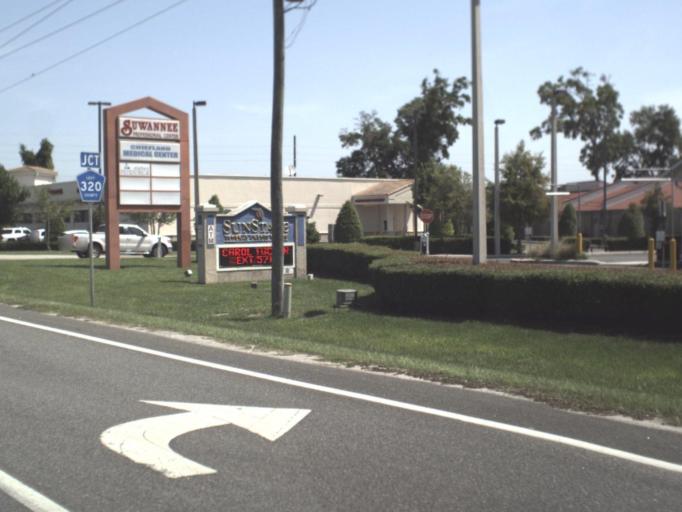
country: US
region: Florida
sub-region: Levy County
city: Chiefland
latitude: 29.5023
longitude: -82.8712
